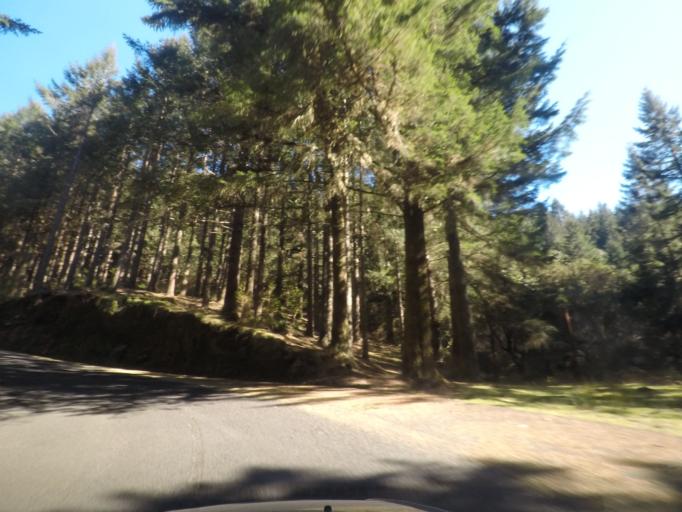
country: PT
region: Madeira
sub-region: Funchal
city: Nossa Senhora do Monte
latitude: 32.7187
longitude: -16.8878
